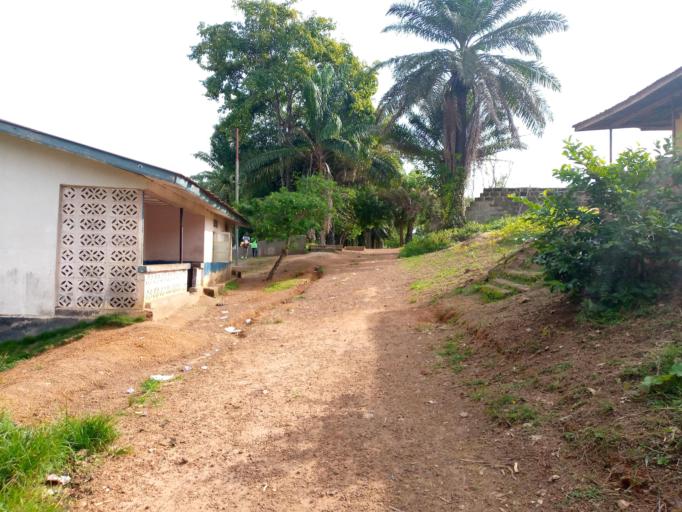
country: SL
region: Northern Province
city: Magburaka
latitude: 8.7190
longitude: -11.9534
